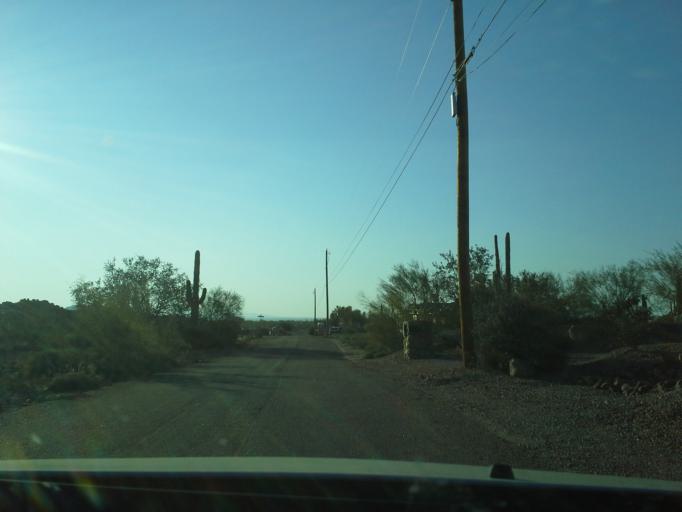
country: US
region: Arizona
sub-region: Pinal County
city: Apache Junction
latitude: 33.3898
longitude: -111.4402
